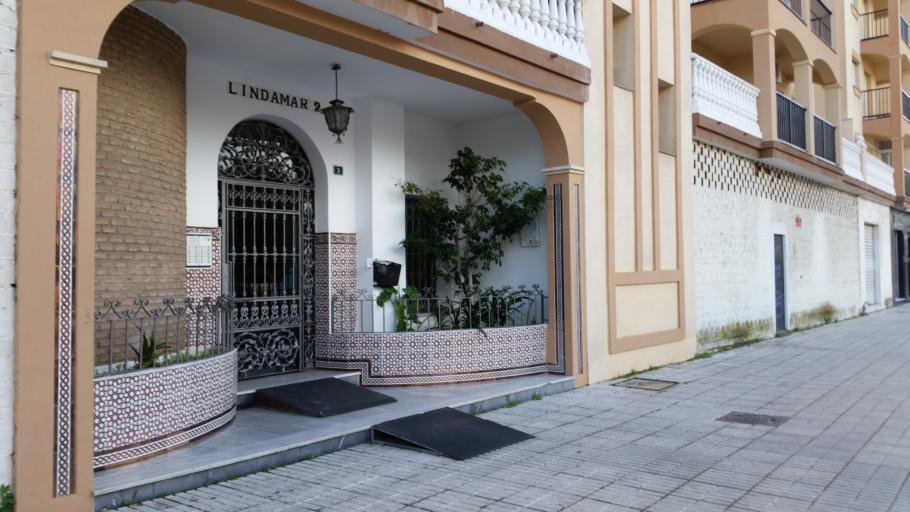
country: ES
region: Andalusia
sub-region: Provincia de Malaga
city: Fuengirola
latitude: 36.5483
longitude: -4.6183
